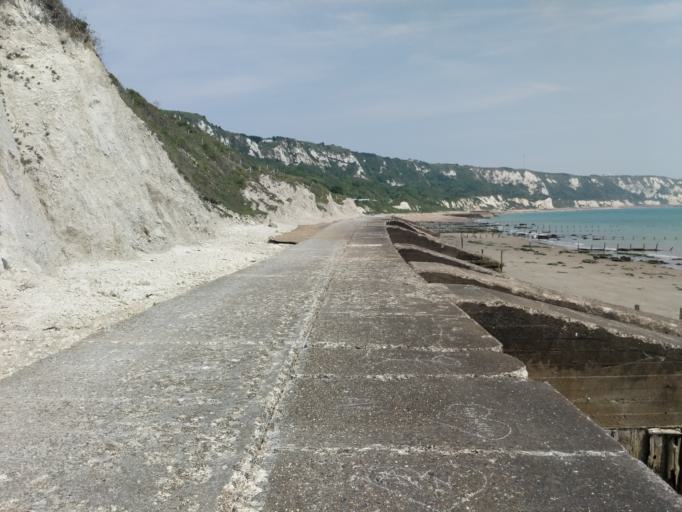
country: GB
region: England
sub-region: Kent
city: Folkestone
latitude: 51.0904
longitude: 1.2030
